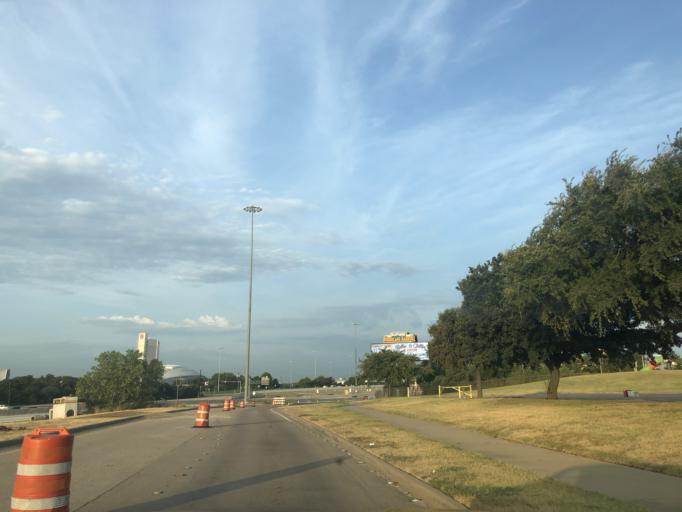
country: US
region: Texas
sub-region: Tarrant County
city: Arlington
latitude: 32.7610
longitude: -97.0776
